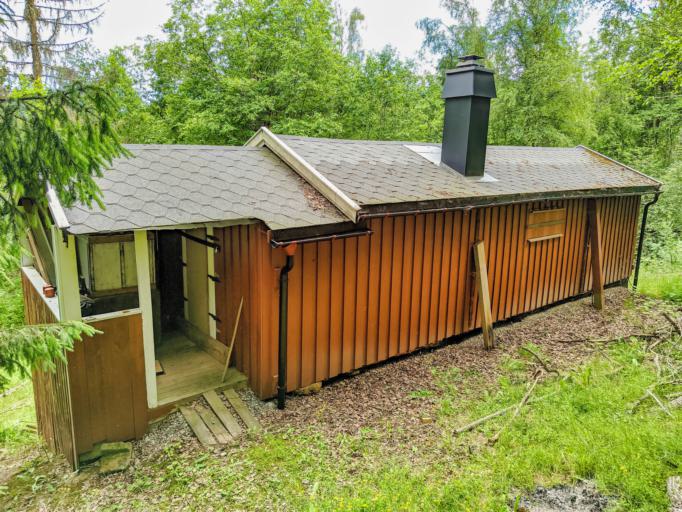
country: NO
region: Akershus
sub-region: Eidsvoll
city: Raholt
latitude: 60.2143
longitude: 11.1510
